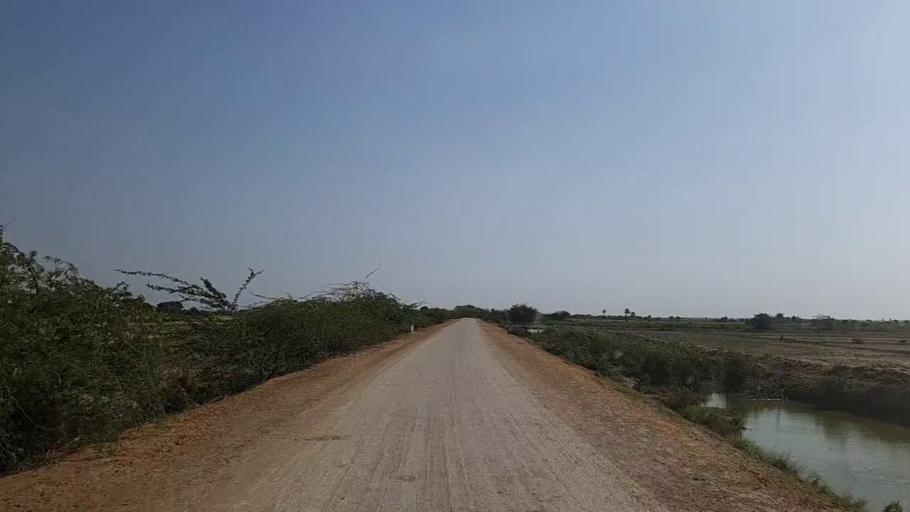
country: PK
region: Sindh
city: Daro Mehar
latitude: 24.7728
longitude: 68.1813
